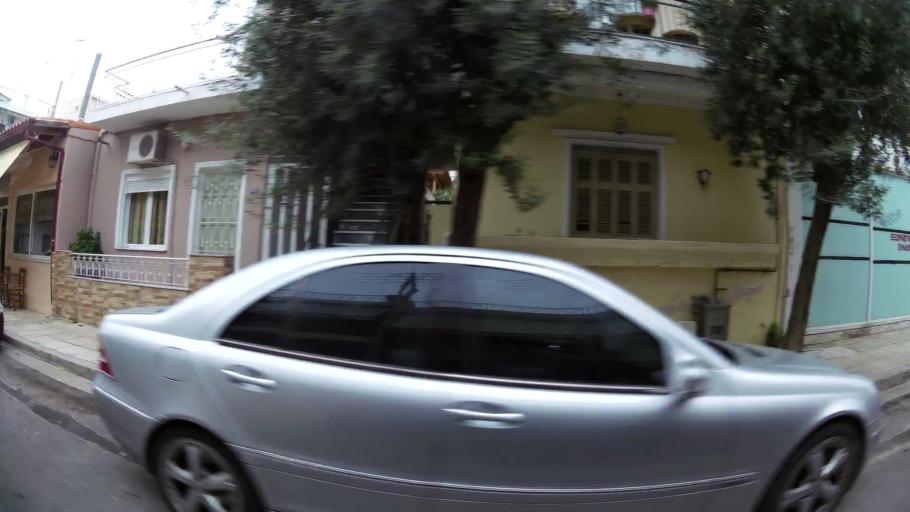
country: GR
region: Attica
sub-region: Nomarchia Athinas
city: Chaidari
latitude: 38.0058
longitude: 23.6741
